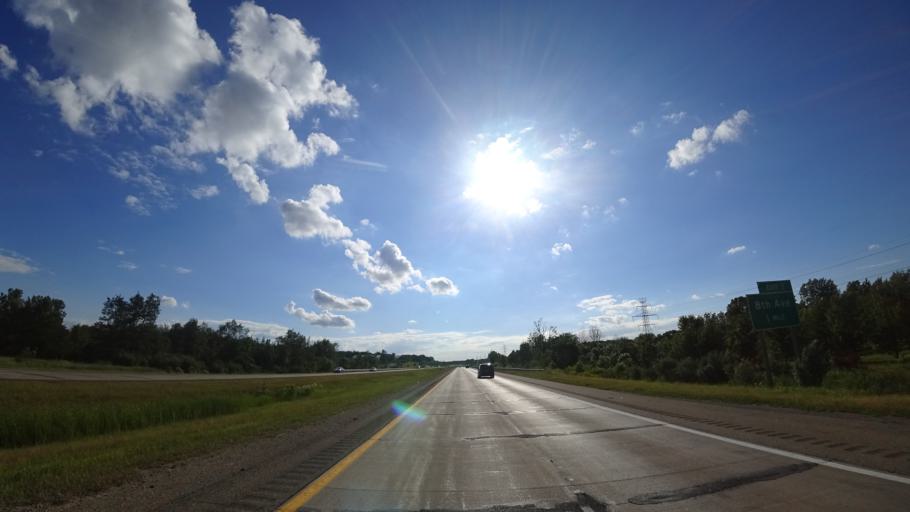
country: US
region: Michigan
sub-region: Kent County
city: Byron Center
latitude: 42.8463
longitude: -85.7730
